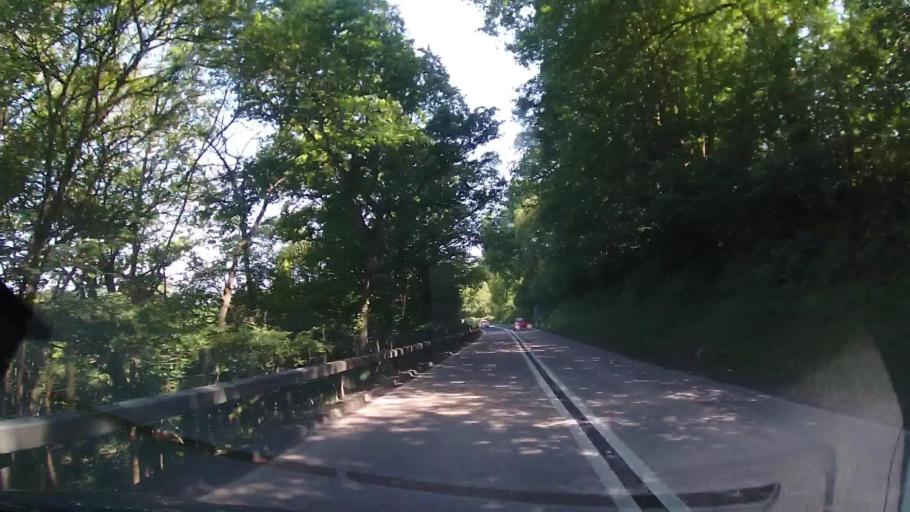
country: GB
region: Wales
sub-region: Sir Powys
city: Llanfyllin
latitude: 52.6527
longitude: -3.3449
